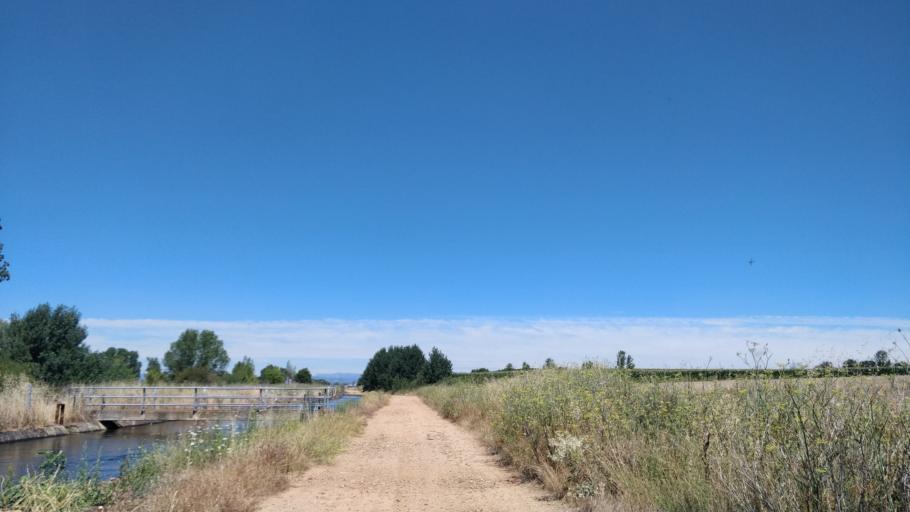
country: ES
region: Castille and Leon
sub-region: Provincia de Leon
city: Bustillo del Paramo
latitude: 42.4786
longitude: -5.8057
